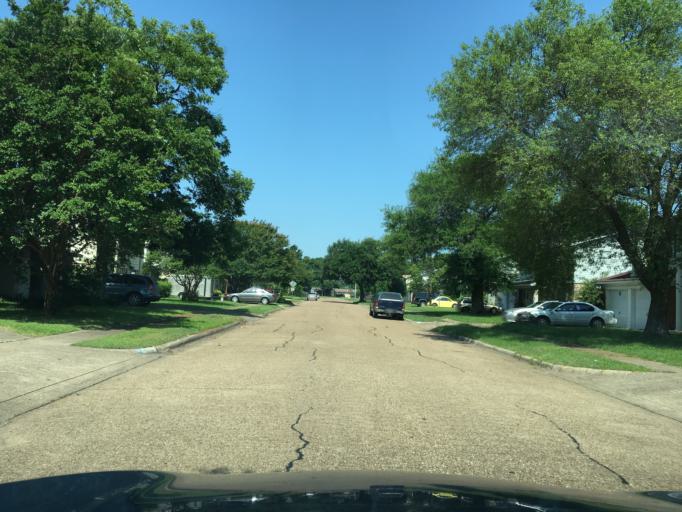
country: US
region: Texas
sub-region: Dallas County
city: Richardson
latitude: 32.9227
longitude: -96.6981
